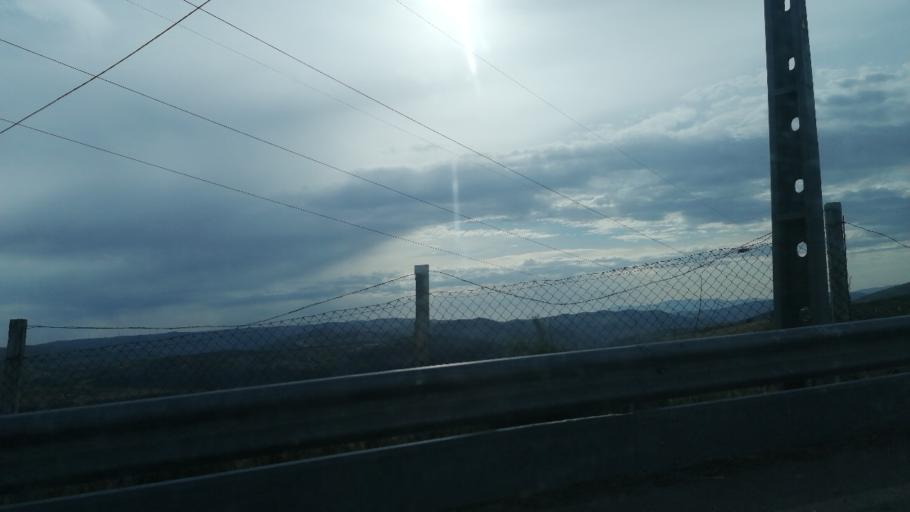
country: PT
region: Viseu
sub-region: Sao Joao da Pesqueira
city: Sao Joao da Pesqueira
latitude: 41.1121
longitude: -7.3892
